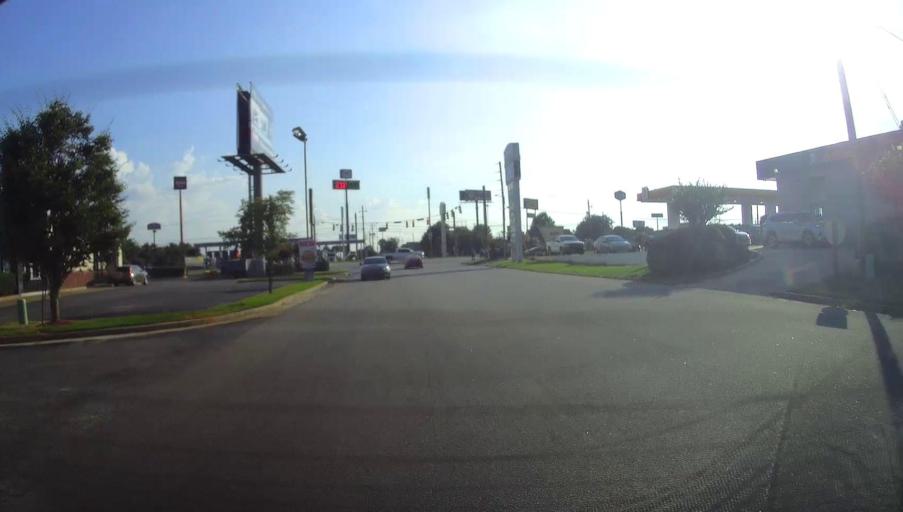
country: US
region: Georgia
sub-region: Houston County
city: Perry
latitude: 32.4703
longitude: -83.7411
